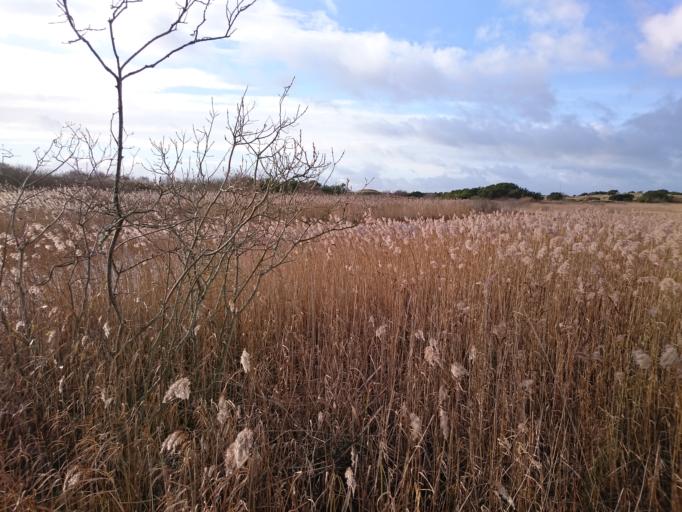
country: DK
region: North Denmark
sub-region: Frederikshavn Kommune
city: Skagen
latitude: 57.7399
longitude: 10.6264
